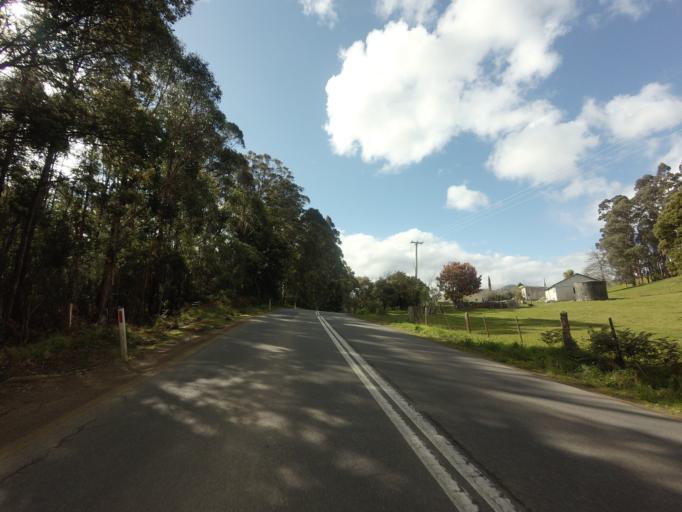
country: AU
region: Tasmania
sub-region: Huon Valley
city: Geeveston
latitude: -43.2208
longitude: 146.9879
